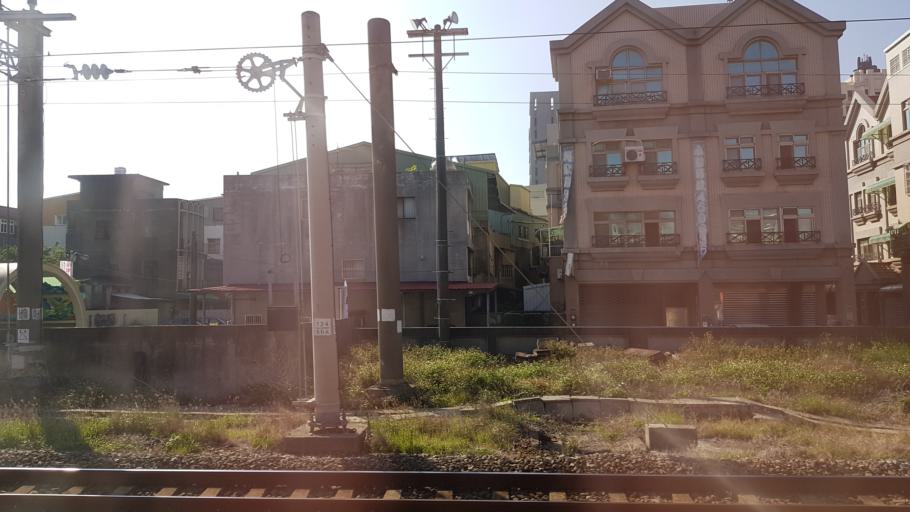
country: TW
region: Taiwan
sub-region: Miaoli
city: Miaoli
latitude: 24.6901
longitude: 120.8808
